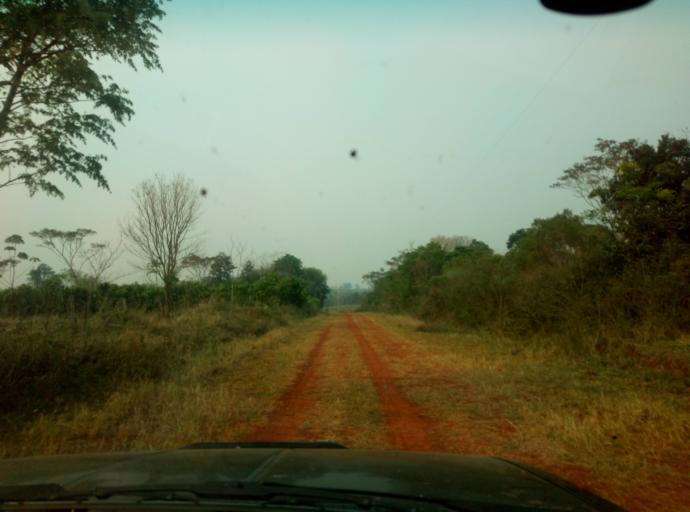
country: PY
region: Caaguazu
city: Carayao
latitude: -25.2080
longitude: -56.2241
